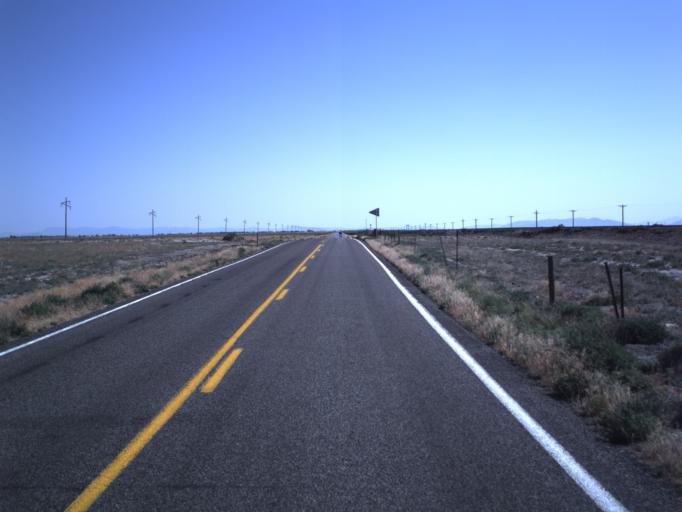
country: US
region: Utah
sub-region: Millard County
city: Delta
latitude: 39.1897
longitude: -112.6945
